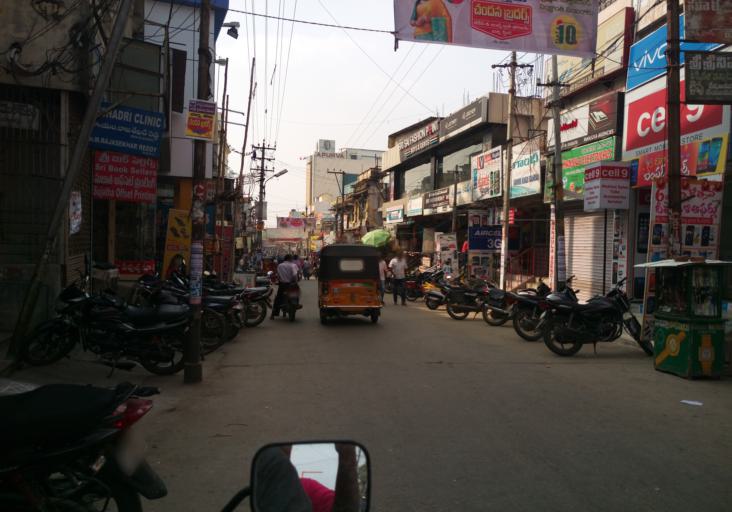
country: IN
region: Andhra Pradesh
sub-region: Chittoor
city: Chittoor
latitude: 13.2172
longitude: 79.1004
